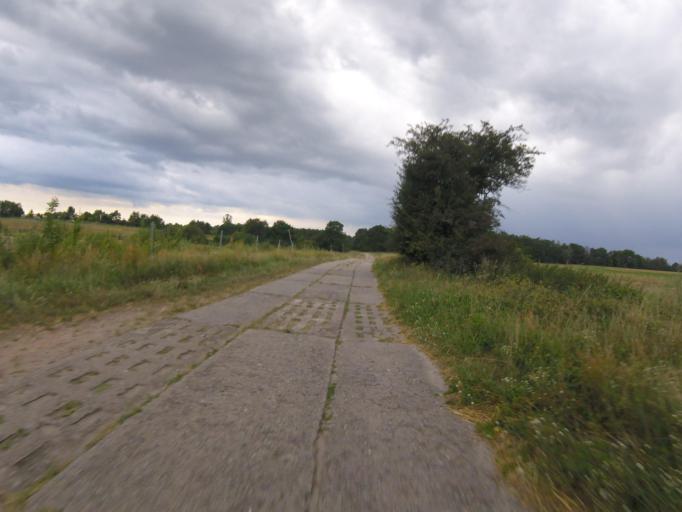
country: DE
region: Brandenburg
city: Mittenwalde
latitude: 52.2809
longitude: 13.5171
